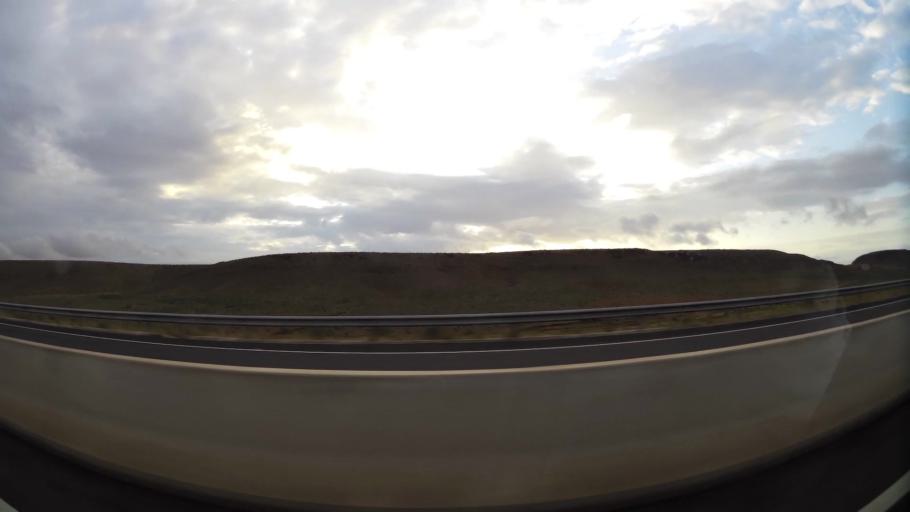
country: MA
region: Oriental
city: Taourirt
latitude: 34.4618
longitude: -3.0438
